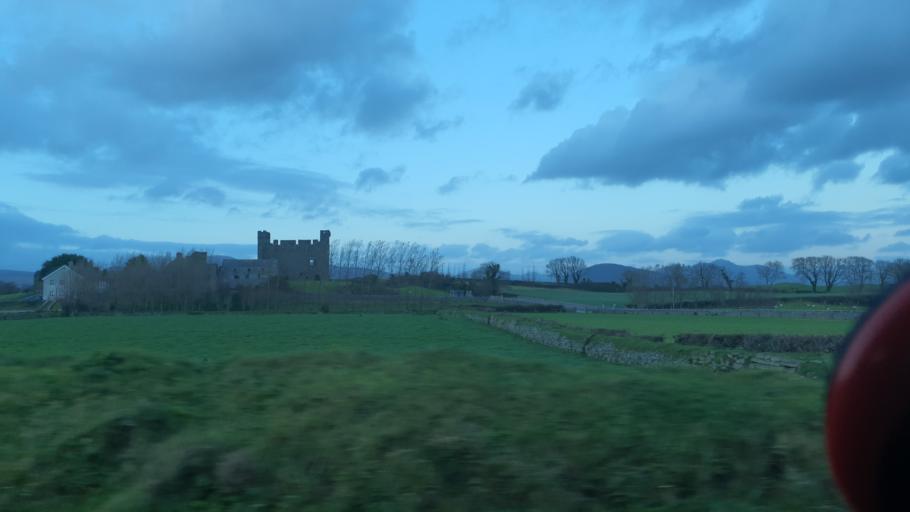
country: IE
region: Leinster
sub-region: Lu
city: Carlingford
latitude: 54.0389
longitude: -6.0972
